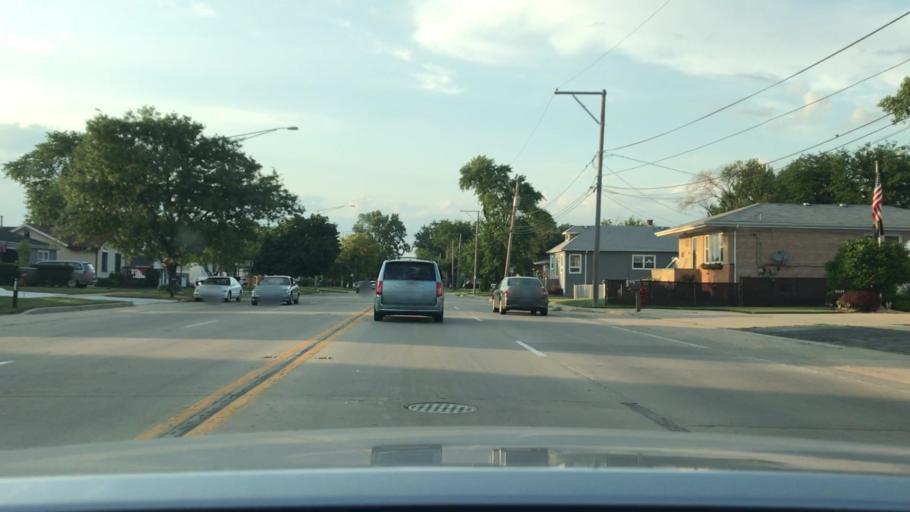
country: US
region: Illinois
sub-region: Cook County
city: Oak Lawn
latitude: 41.7275
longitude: -87.7606
